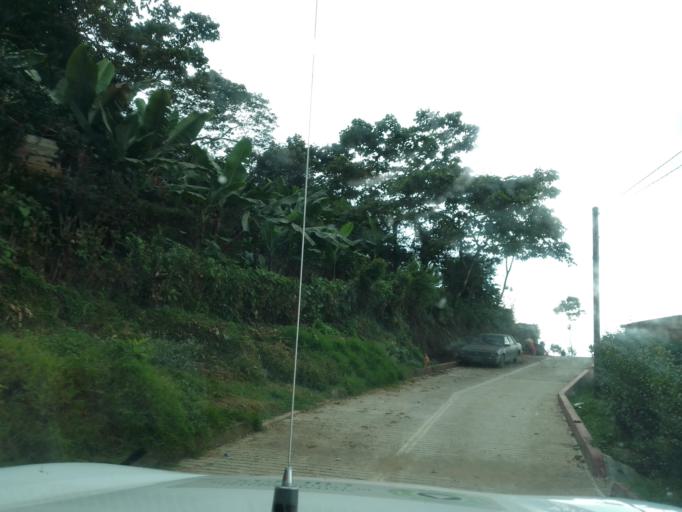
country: MX
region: Chiapas
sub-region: Union Juarez
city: Santo Domingo
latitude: 15.0670
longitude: -92.1140
